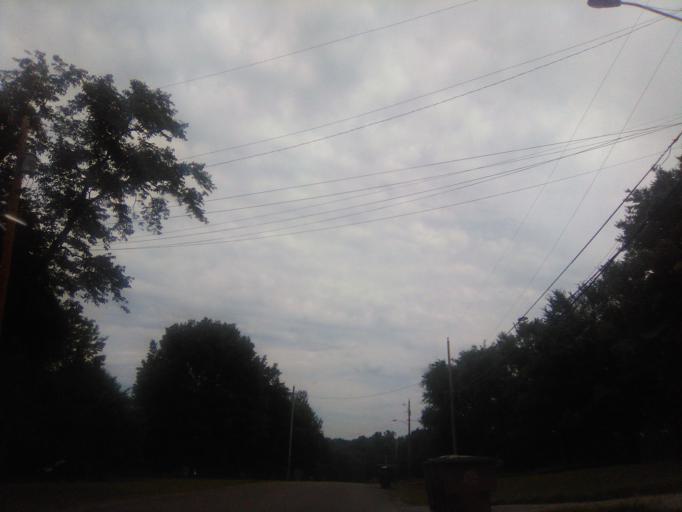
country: US
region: Tennessee
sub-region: Davidson County
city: Belle Meade
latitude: 36.1145
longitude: -86.8951
